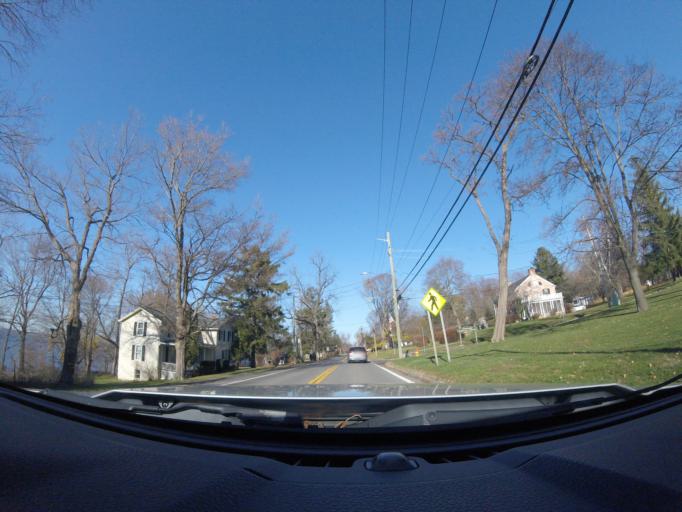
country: US
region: New York
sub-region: Cayuga County
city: Union Springs
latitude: 42.7470
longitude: -76.7002
